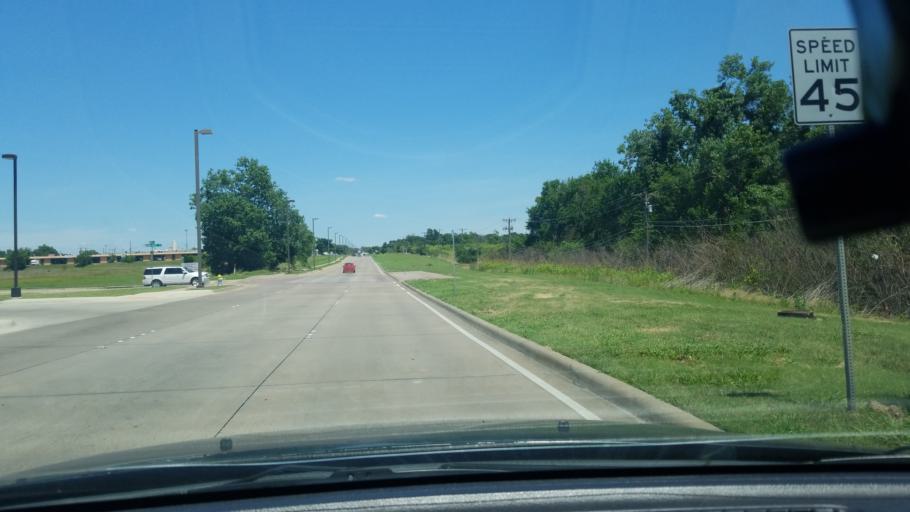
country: US
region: Texas
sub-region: Dallas County
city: Mesquite
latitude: 32.7675
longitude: -96.6199
